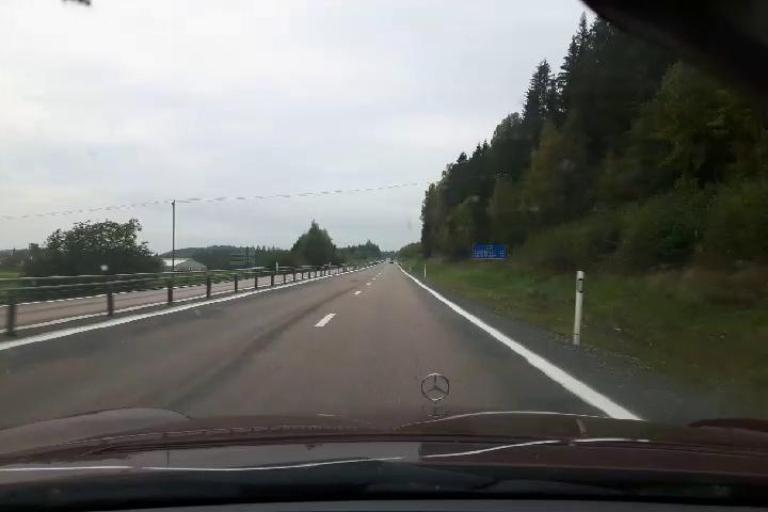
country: SE
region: Vaesternorrland
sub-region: Haernoesands Kommun
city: Haernoesand
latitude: 62.8506
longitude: 18.0060
